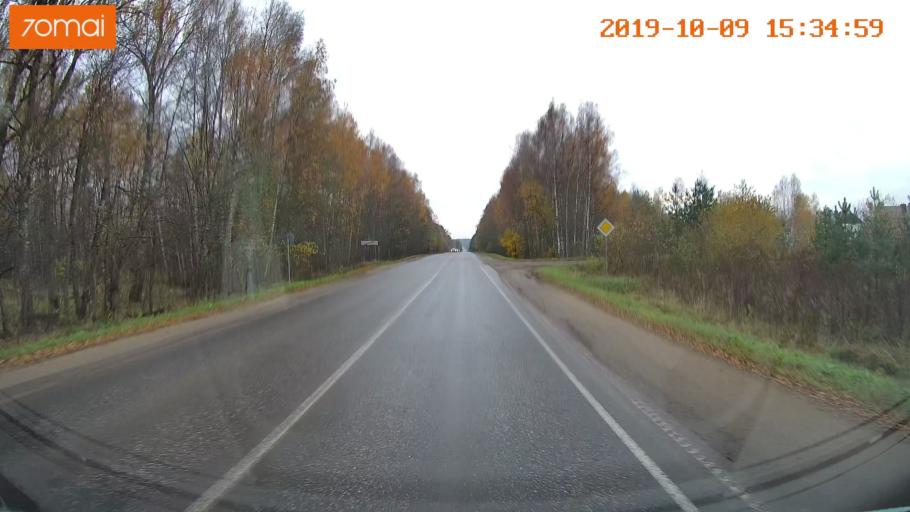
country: RU
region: Kostroma
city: Oktyabr'skiy
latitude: 57.9365
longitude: 41.2361
